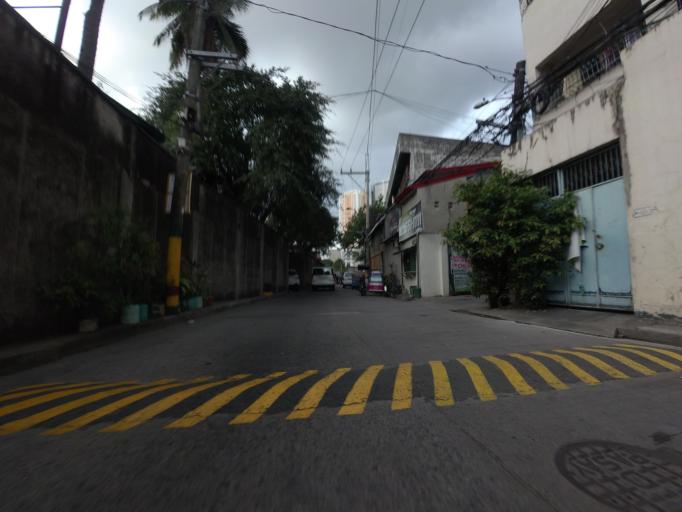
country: PH
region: Metro Manila
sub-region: City of Manila
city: Port Area
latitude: 14.5579
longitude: 120.9948
